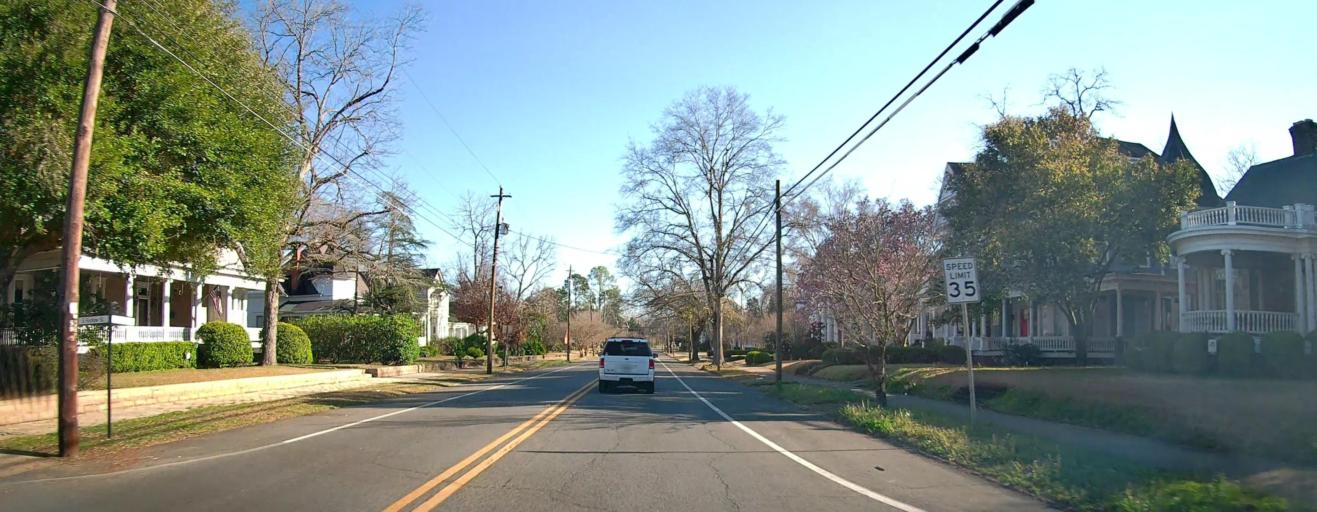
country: US
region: Georgia
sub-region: Sumter County
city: Americus
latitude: 32.0641
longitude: -84.2295
